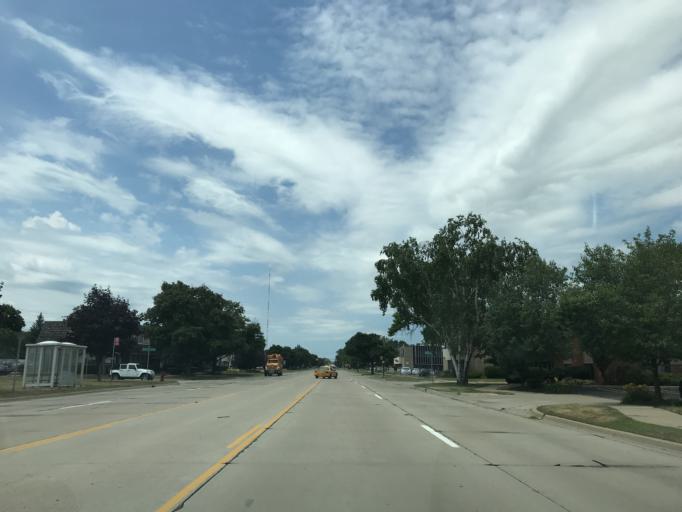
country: US
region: Michigan
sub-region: Oakland County
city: Southfield
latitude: 42.4733
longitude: -83.2266
